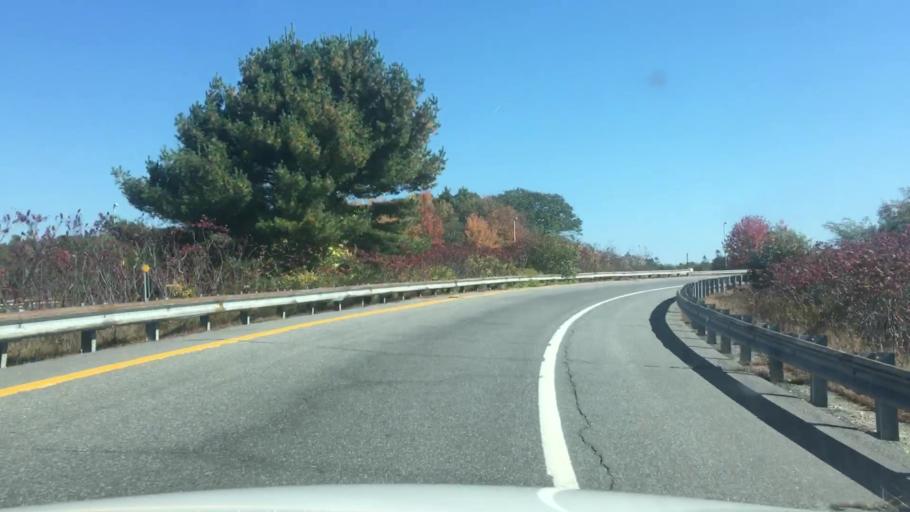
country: US
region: Maine
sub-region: Sagadahoc County
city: Bath
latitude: 43.9163
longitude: -69.8603
